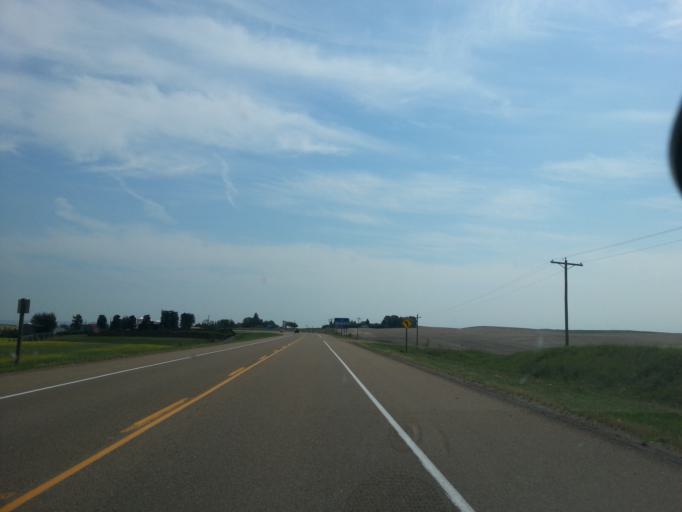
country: CA
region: Alberta
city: Three Hills
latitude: 51.4160
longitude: -112.7372
